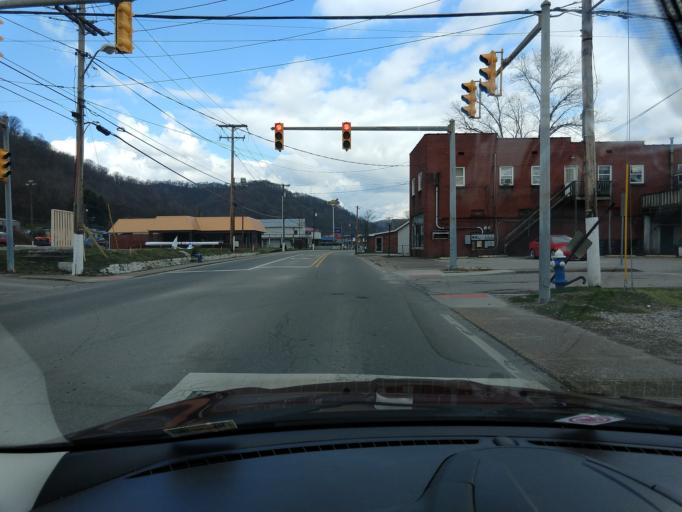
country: US
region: West Virginia
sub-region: Kanawha County
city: Marmet
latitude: 38.2431
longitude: -81.5659
